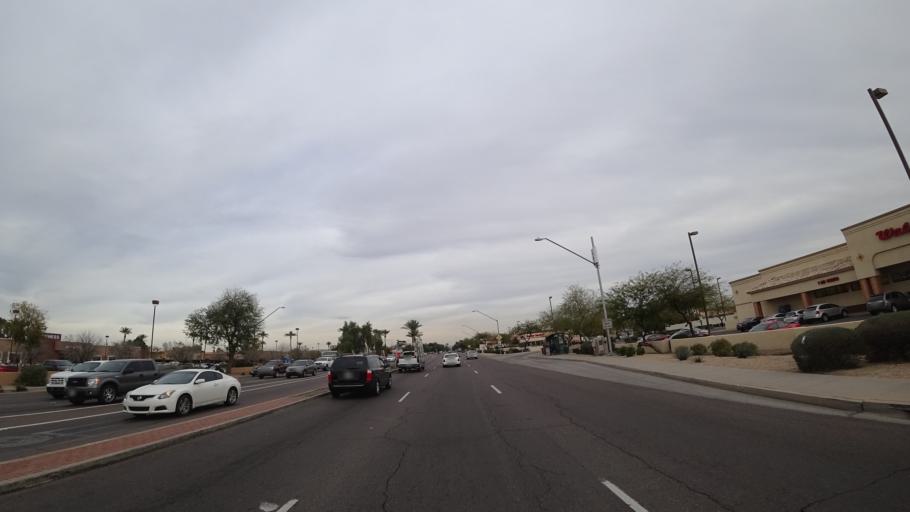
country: US
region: Arizona
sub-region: Maricopa County
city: Glendale
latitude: 33.5818
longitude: -112.1859
